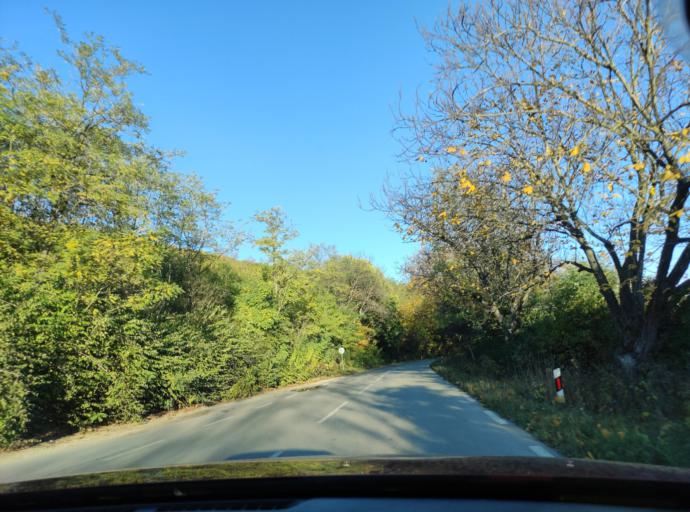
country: BG
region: Montana
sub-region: Obshtina Montana
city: Montana
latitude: 43.4073
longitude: 23.0587
